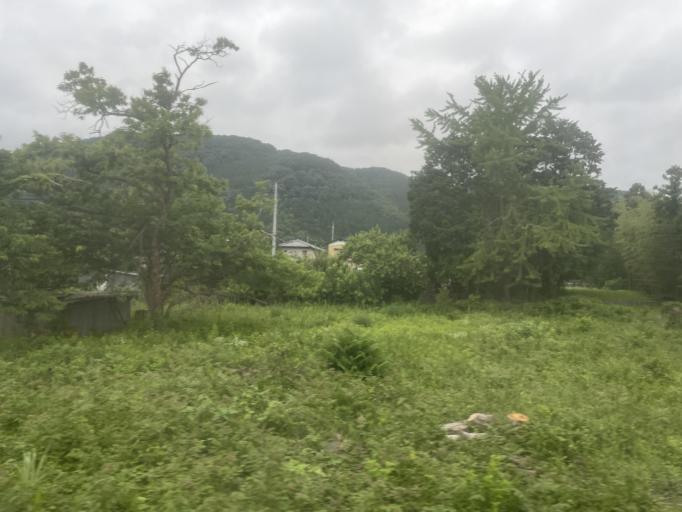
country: JP
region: Saitama
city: Kodamacho-kodamaminami
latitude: 36.1072
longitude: 139.1105
